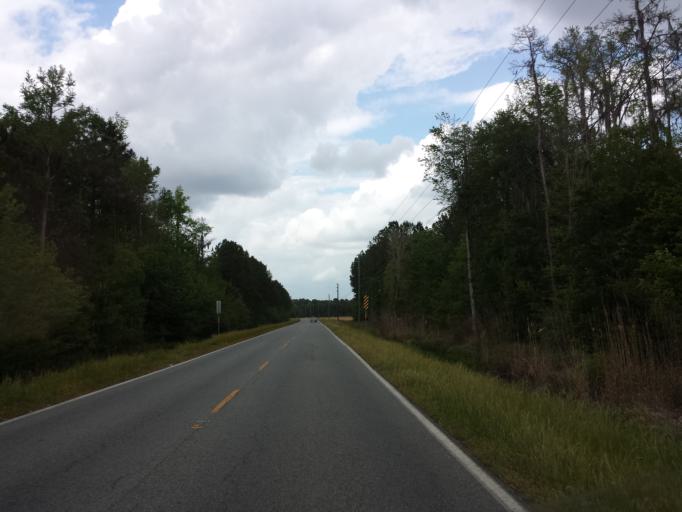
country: US
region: Georgia
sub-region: Cook County
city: Adel
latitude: 31.0961
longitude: -83.4090
